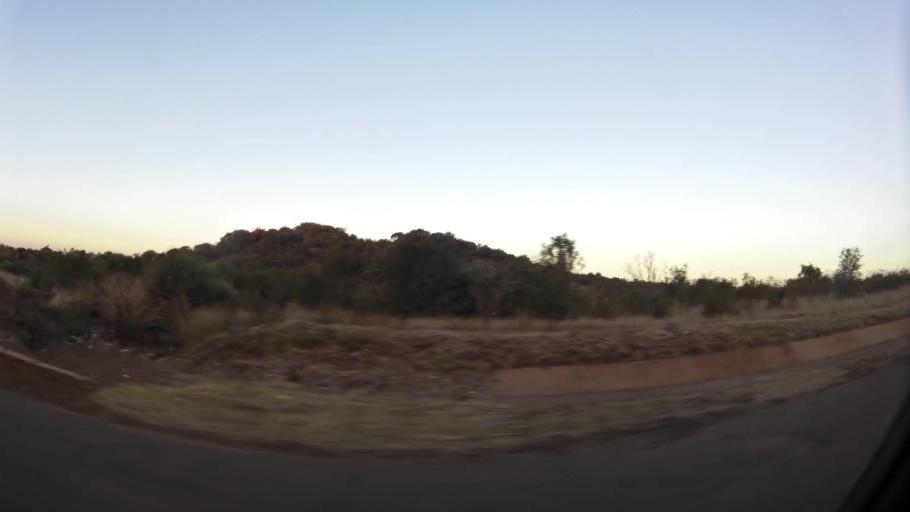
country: ZA
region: North-West
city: Ga-Rankuwa
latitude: -25.6046
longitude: 28.0393
